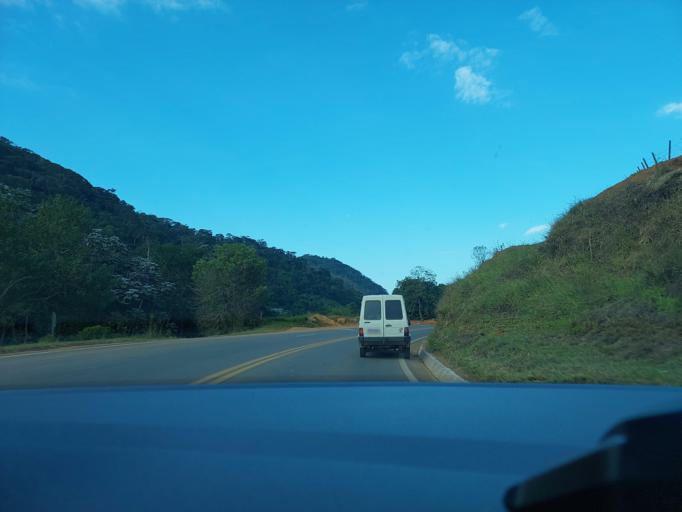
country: BR
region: Minas Gerais
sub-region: Muriae
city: Muriae
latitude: -21.0750
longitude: -42.4996
